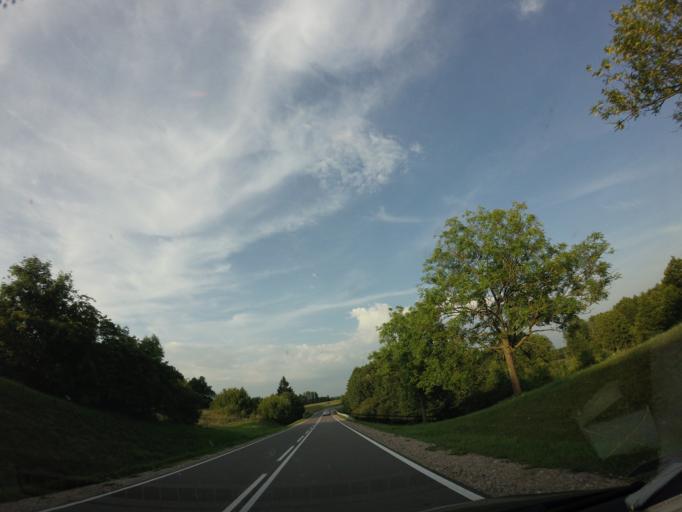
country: PL
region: Podlasie
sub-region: Powiat sejnenski
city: Sejny
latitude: 54.1251
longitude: 23.4390
